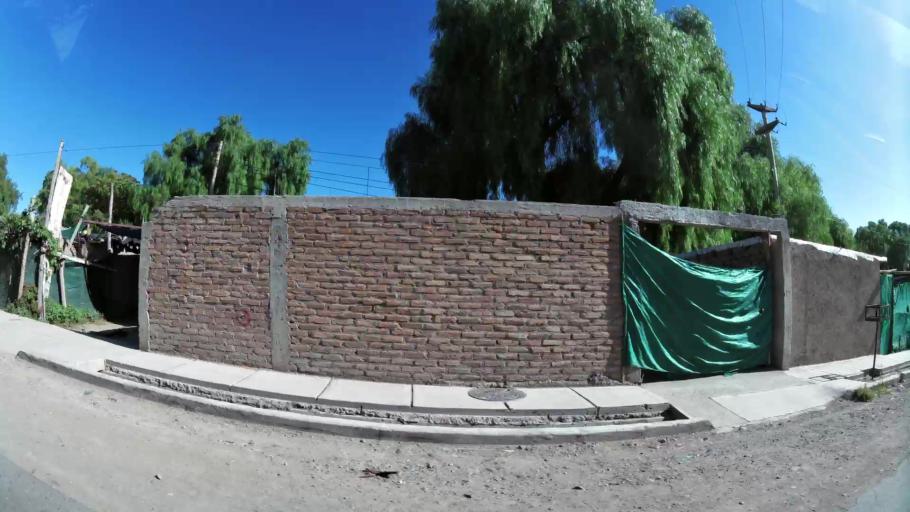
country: AR
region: Mendoza
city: Mendoza
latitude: -32.8752
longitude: -68.8717
